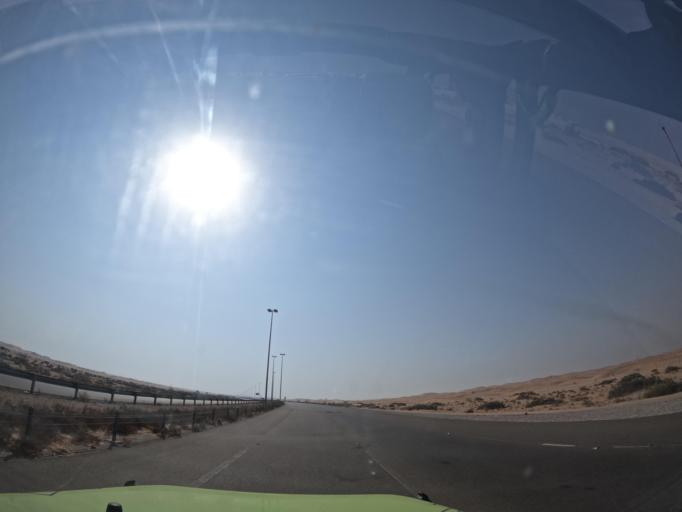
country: OM
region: Al Buraimi
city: Al Buraymi
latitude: 24.5190
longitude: 55.5555
